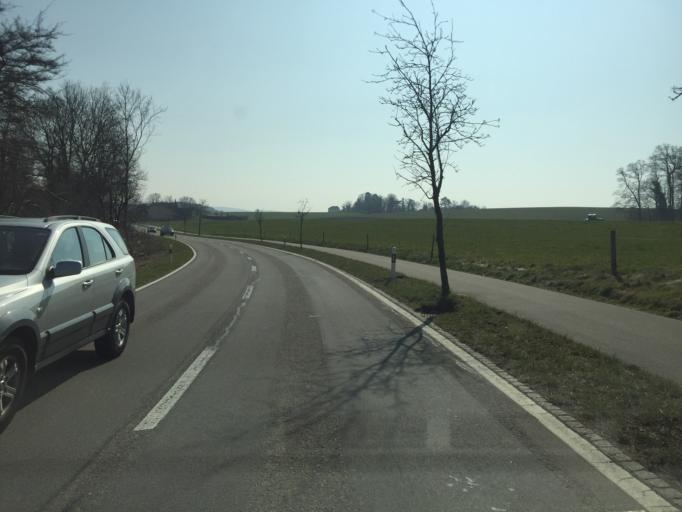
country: CH
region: Thurgau
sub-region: Frauenfeld District
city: Huttwilen
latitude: 47.6007
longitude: 8.8790
